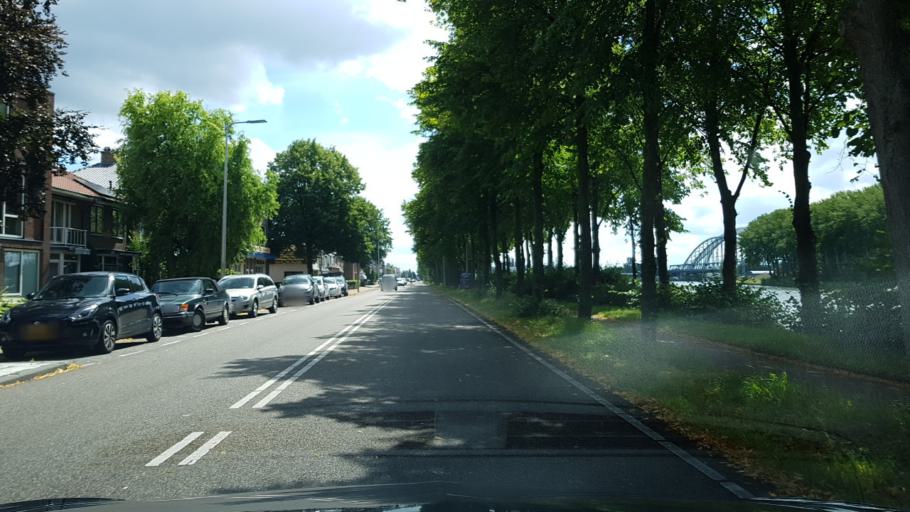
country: NL
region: Utrecht
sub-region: Stichtse Vecht
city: Maarssen
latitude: 52.1165
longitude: 5.0727
